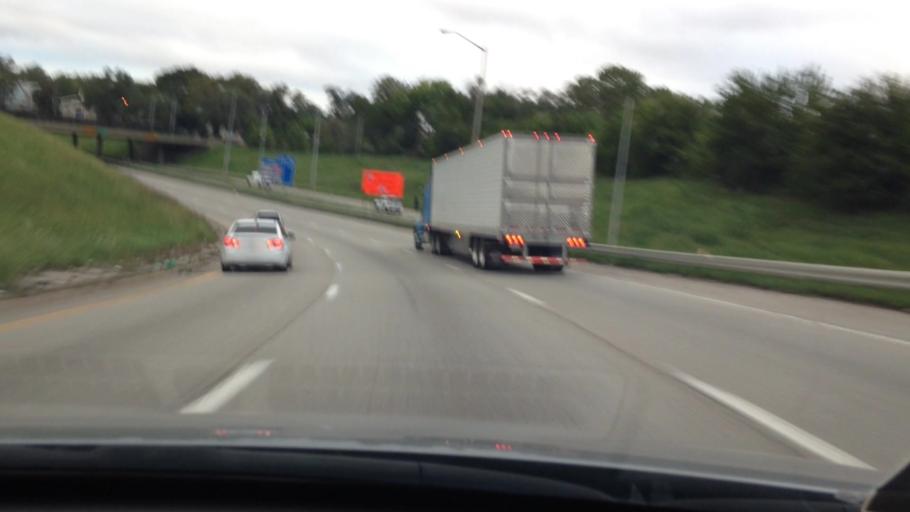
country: US
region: Missouri
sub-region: Jackson County
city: Kansas City
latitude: 39.0952
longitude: -94.5433
